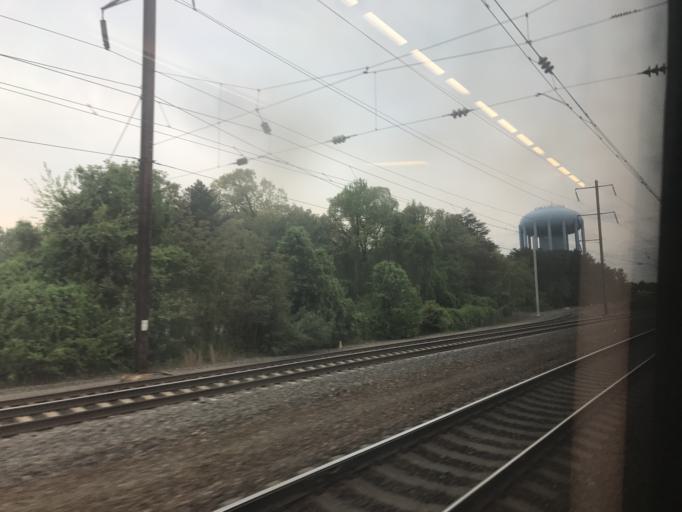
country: US
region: Maryland
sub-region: Anne Arundel County
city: Odenton
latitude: 39.0808
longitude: -76.7106
